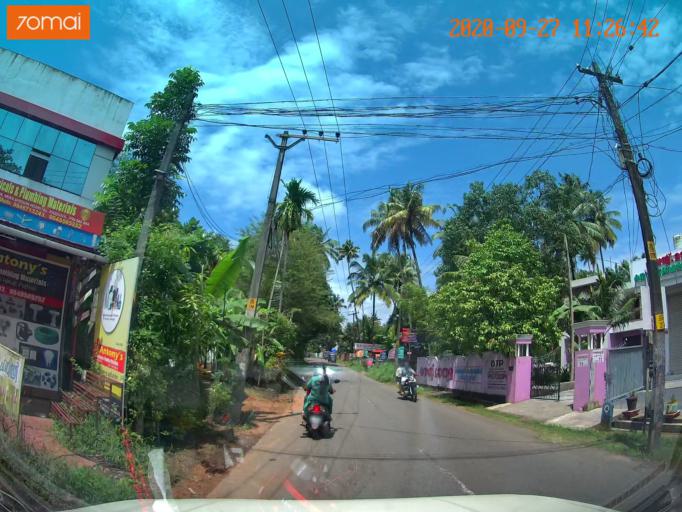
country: IN
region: Kerala
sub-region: Thrissur District
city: Thanniyam
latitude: 10.4167
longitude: 76.1534
